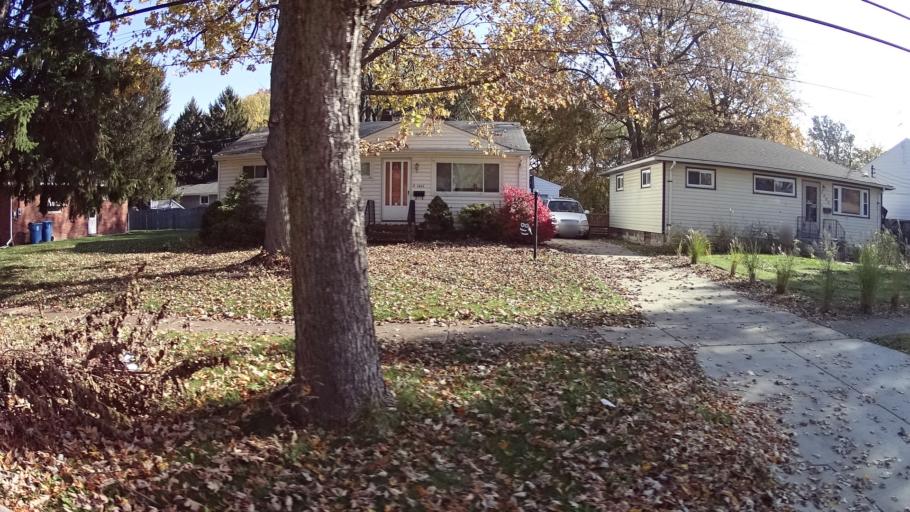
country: US
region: Ohio
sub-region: Lorain County
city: Lorain
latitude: 41.4679
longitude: -82.1463
